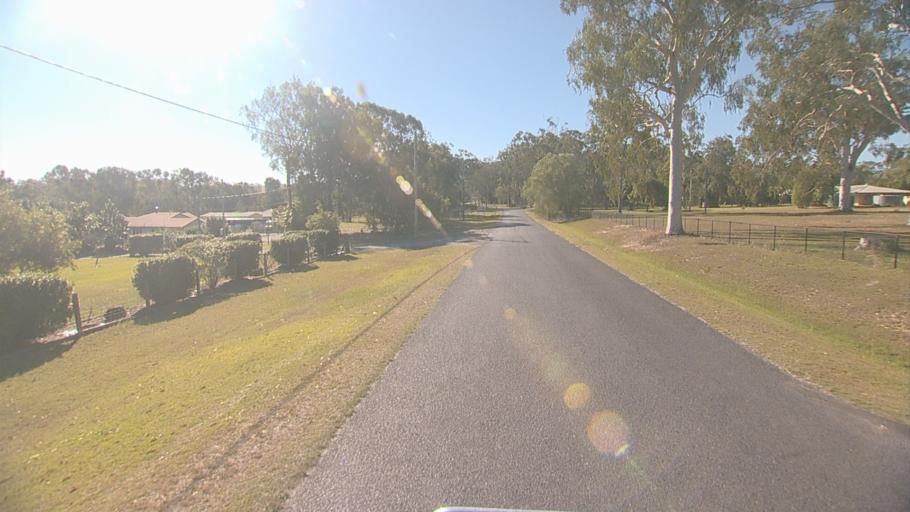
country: AU
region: Queensland
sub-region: Logan
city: Chambers Flat
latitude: -27.7362
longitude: 153.0778
